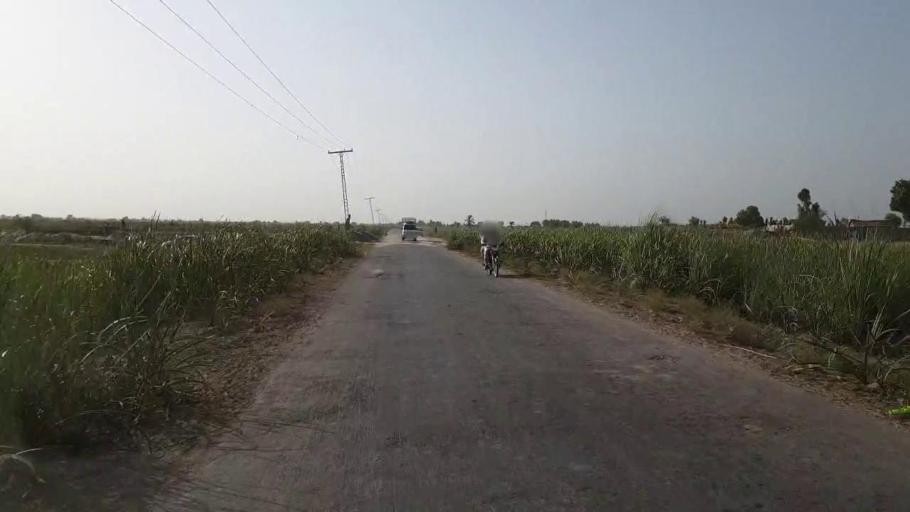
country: PK
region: Sindh
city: Jam Sahib
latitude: 26.4121
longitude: 68.8742
